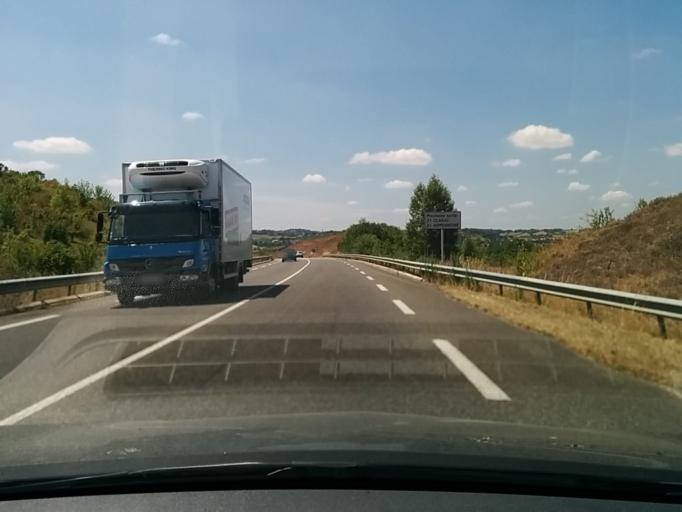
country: FR
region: Midi-Pyrenees
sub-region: Departement du Gers
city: Auch
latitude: 43.6663
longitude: 0.6080
